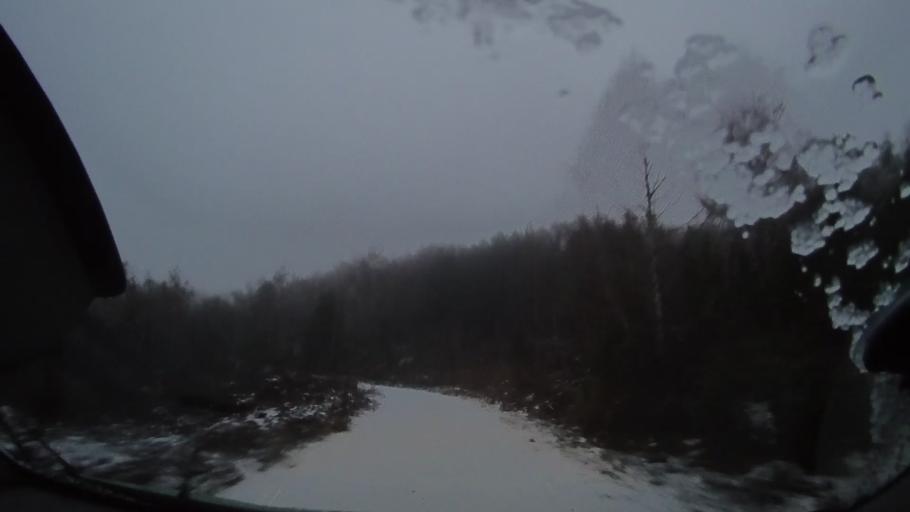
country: RO
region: Alba
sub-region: Comuna Avram Iancu
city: Avram Iancu
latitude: 46.3094
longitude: 22.7997
